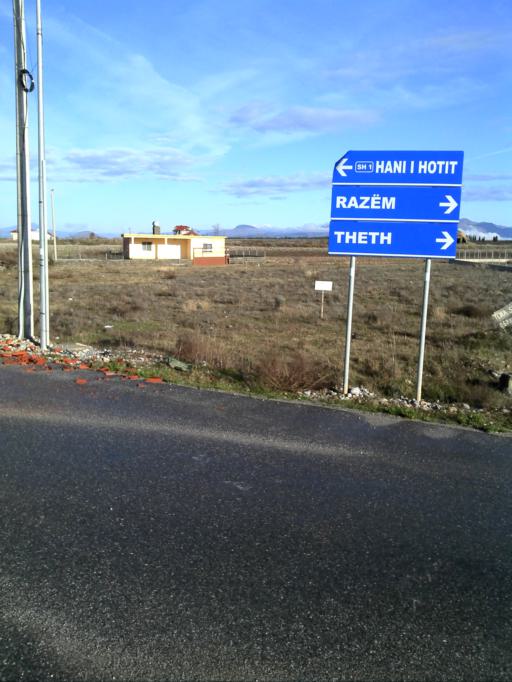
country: AL
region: Shkoder
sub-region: Rrethi i Malesia e Madhe
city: Koplik
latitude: 42.2202
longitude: 19.4457
